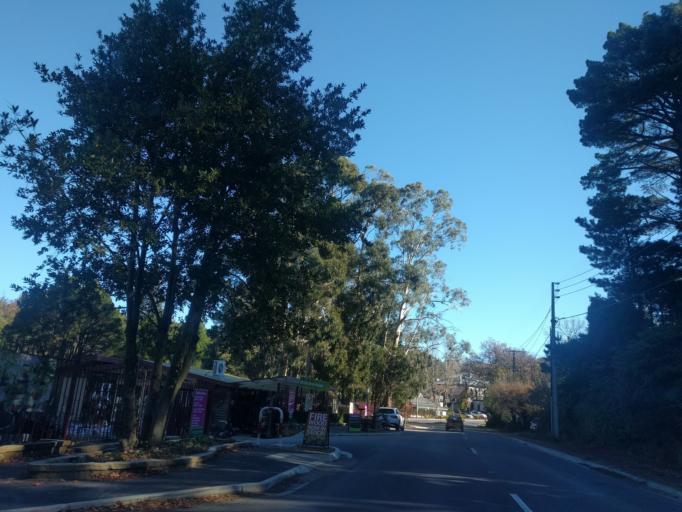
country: AU
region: South Australia
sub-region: Adelaide Hills
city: Crafers
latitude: -34.9973
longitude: 138.7062
